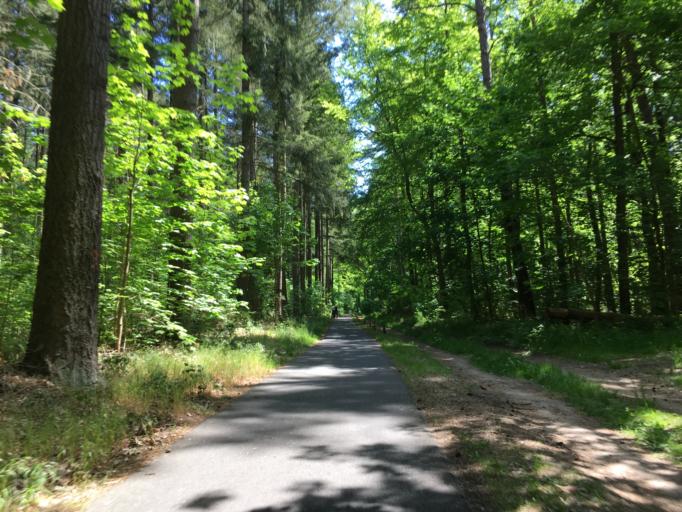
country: DE
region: Brandenburg
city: Chorin
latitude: 52.8510
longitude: 13.8792
